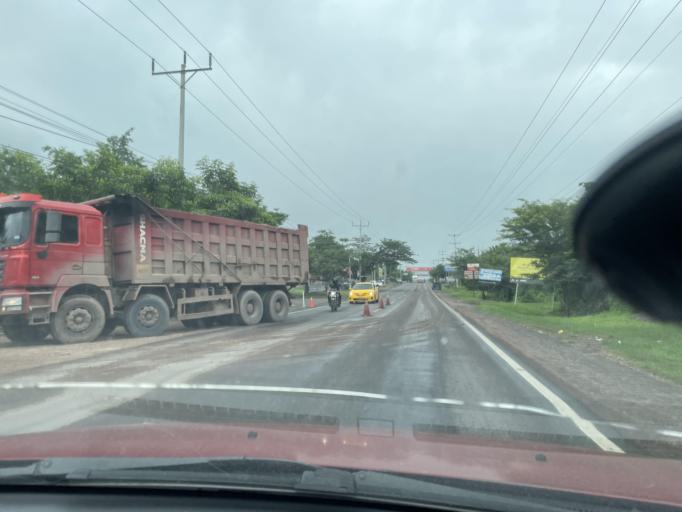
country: SV
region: San Miguel
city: San Miguel
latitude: 13.5093
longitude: -88.1524
